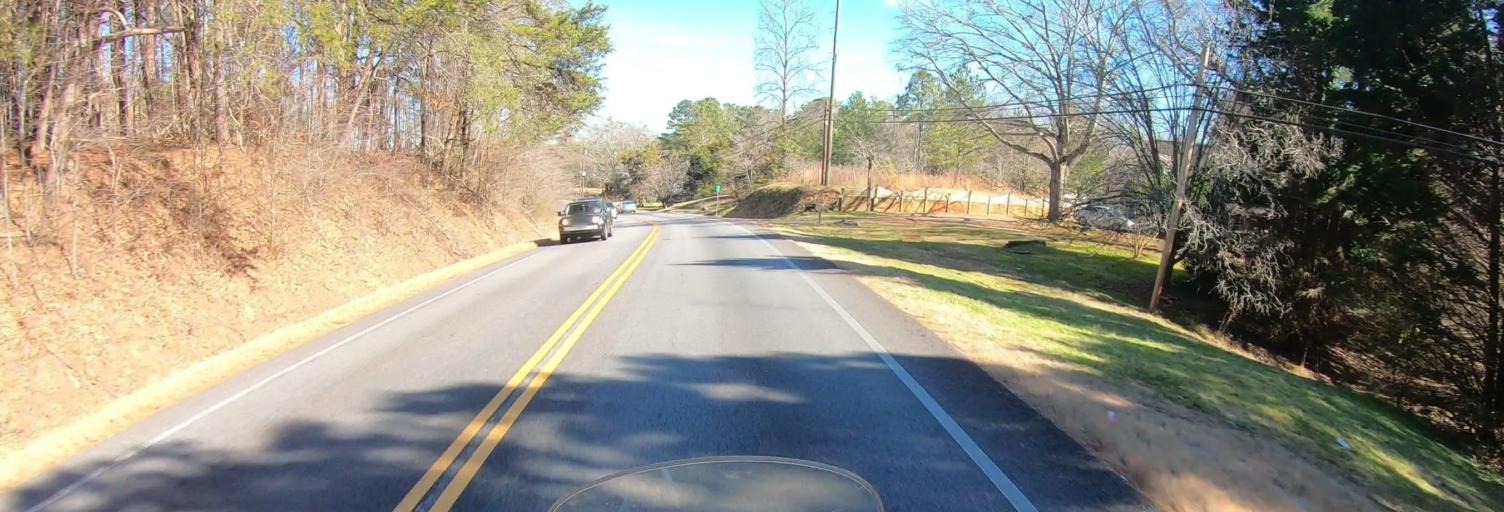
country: US
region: Georgia
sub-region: Hall County
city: Oakwood
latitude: 34.2684
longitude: -83.9217
